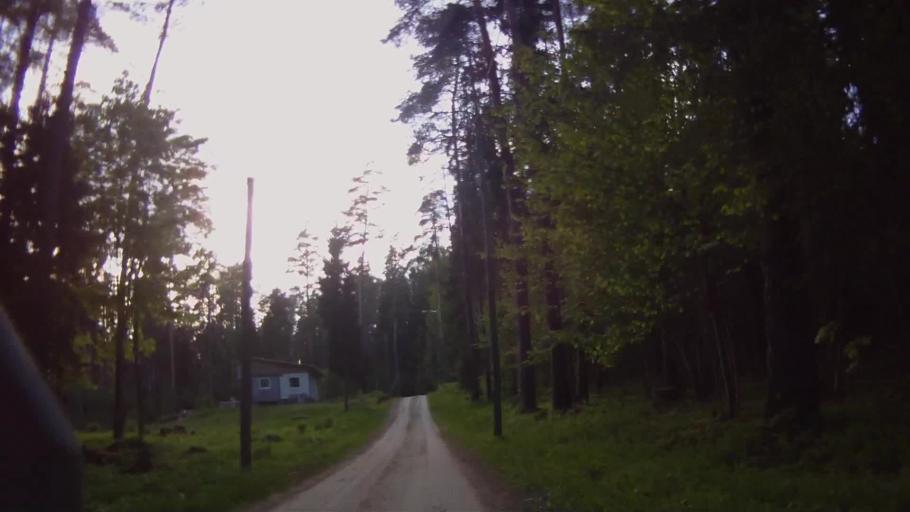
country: LV
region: Baldone
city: Baldone
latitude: 56.7491
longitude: 24.4198
